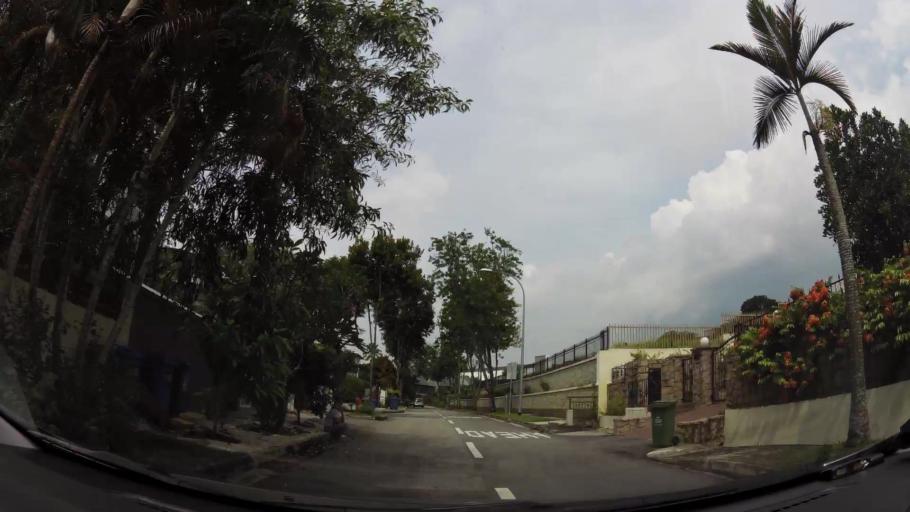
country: MY
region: Johor
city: Kampung Pasir Gudang Baru
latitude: 1.3652
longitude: 103.9738
